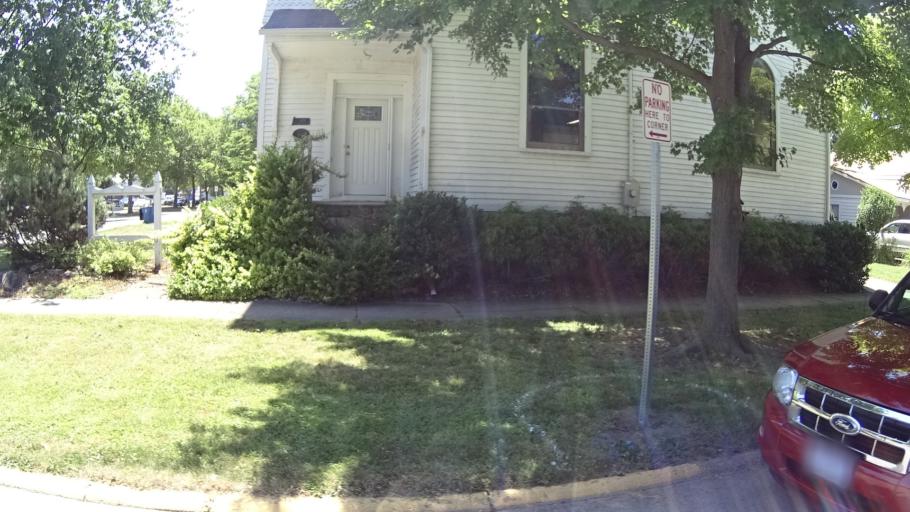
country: US
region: Ohio
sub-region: Erie County
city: Huron
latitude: 41.3934
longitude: -82.5576
